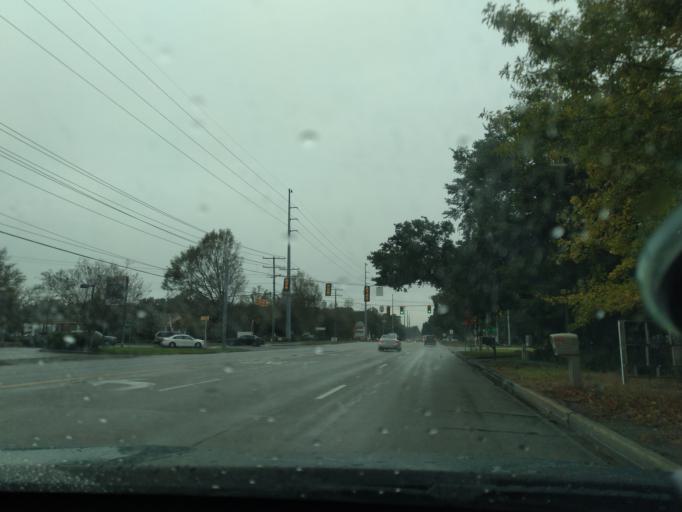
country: US
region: South Carolina
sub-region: Charleston County
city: Folly Beach
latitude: 32.7157
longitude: -79.9654
